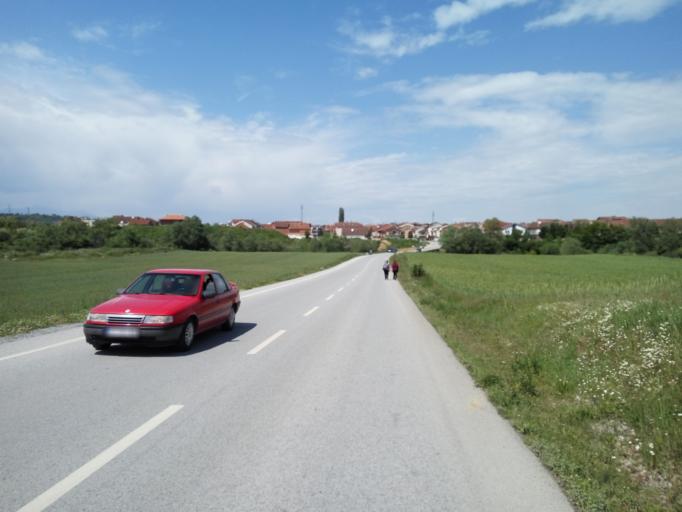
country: XK
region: Gjakova
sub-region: Komuna e Gjakoves
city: Gjakove
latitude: 42.3636
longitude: 20.4355
